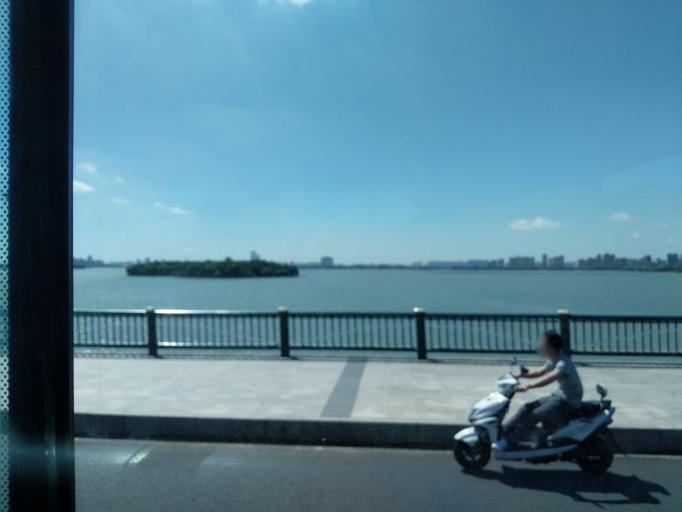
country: CN
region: Jiangsu Sheng
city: Weiting
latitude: 31.3266
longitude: 120.6848
